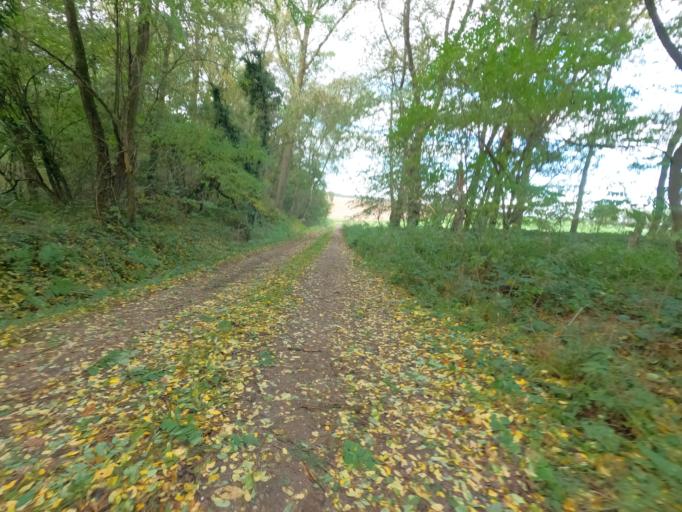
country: DE
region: North Rhine-Westphalia
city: Erkelenz
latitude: 51.0446
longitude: 6.2790
